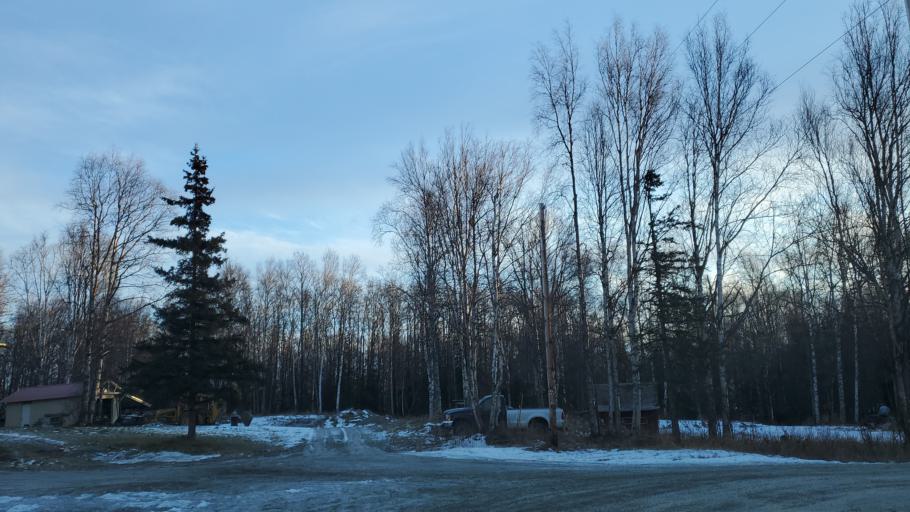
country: US
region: Alaska
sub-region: Matanuska-Susitna Borough
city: Lakes
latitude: 61.6530
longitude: -149.3165
